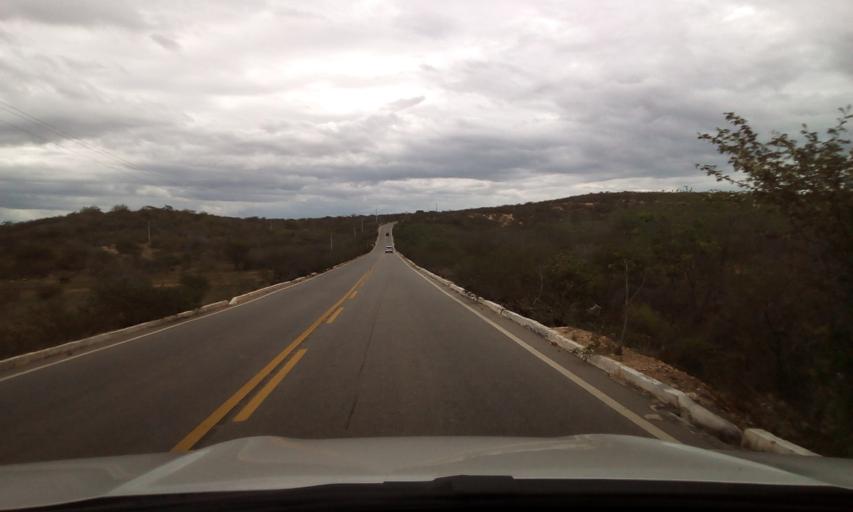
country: BR
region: Paraiba
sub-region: Picui
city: Picui
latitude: -6.5241
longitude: -36.3250
